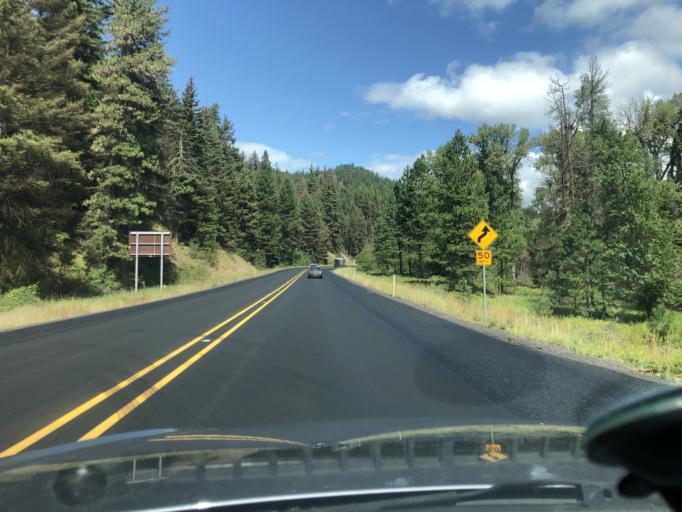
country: US
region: Washington
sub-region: Kittitas County
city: Cle Elum
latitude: 47.2968
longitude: -120.7005
